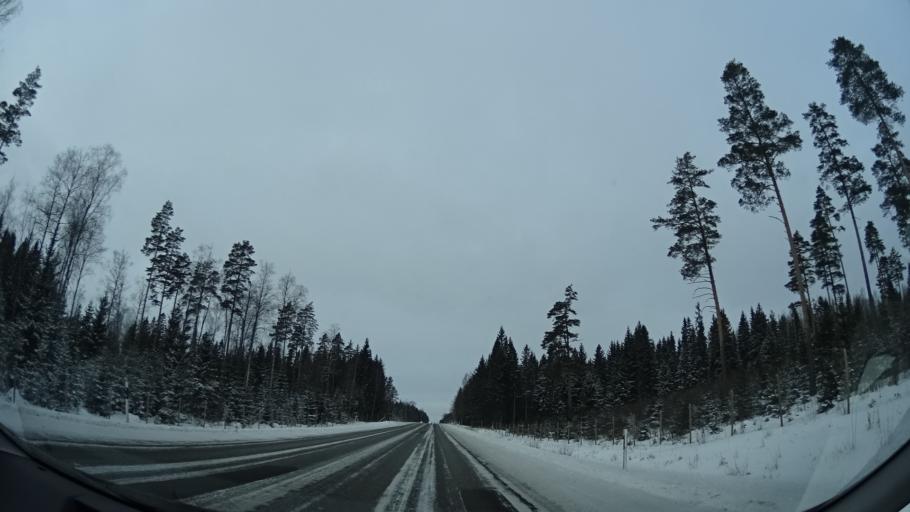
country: FI
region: Uusimaa
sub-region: Helsinki
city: Kaerkoelae
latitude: 60.6253
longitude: 23.9672
